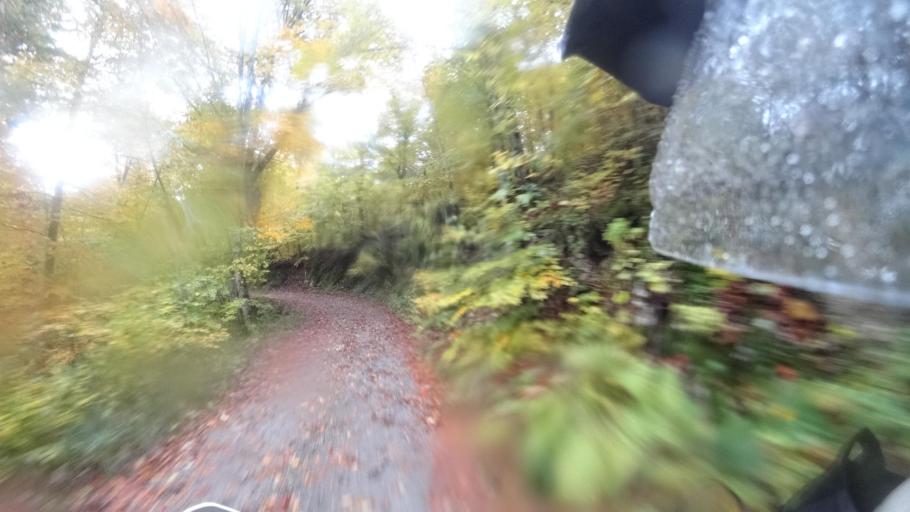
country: HR
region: Primorsko-Goranska
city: Vrbovsko
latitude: 45.3523
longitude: 15.0721
